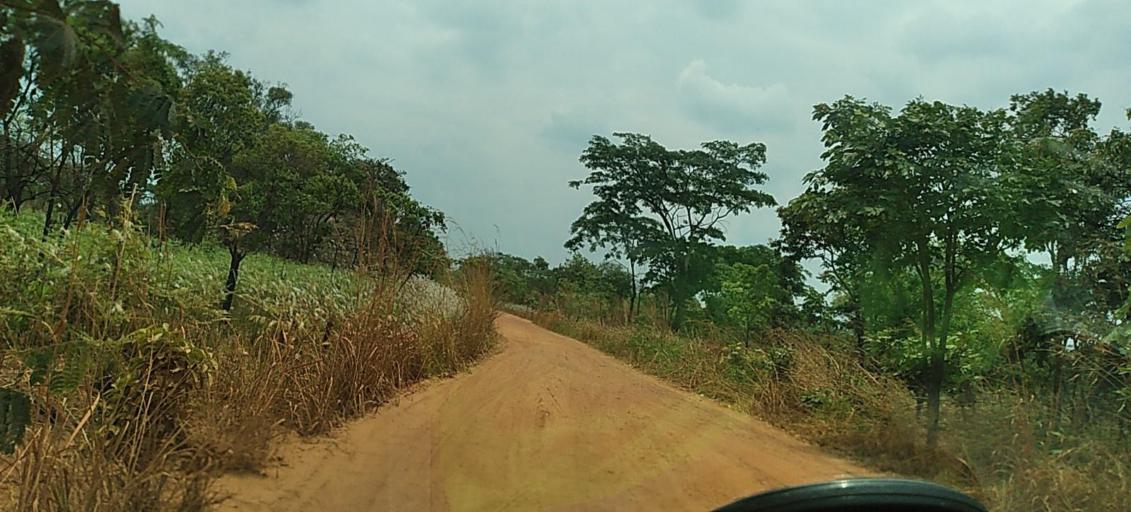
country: ZM
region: North-Western
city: Kansanshi
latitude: -12.0644
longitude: 26.3519
